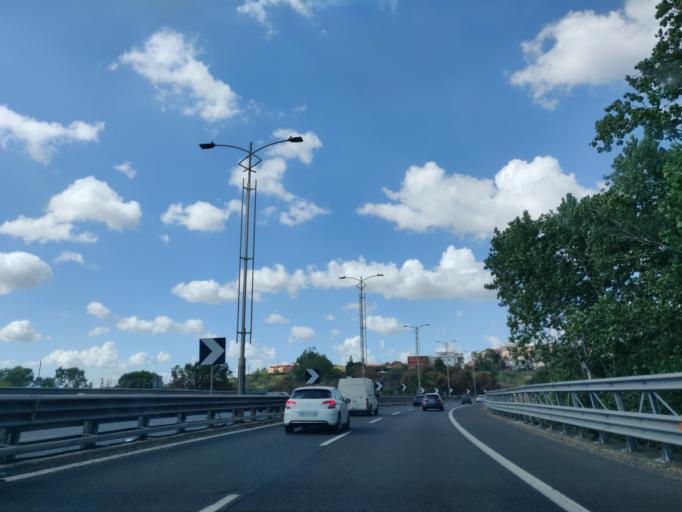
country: IT
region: Latium
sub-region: Citta metropolitana di Roma Capitale
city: Vitinia
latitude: 41.8289
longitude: 12.4197
